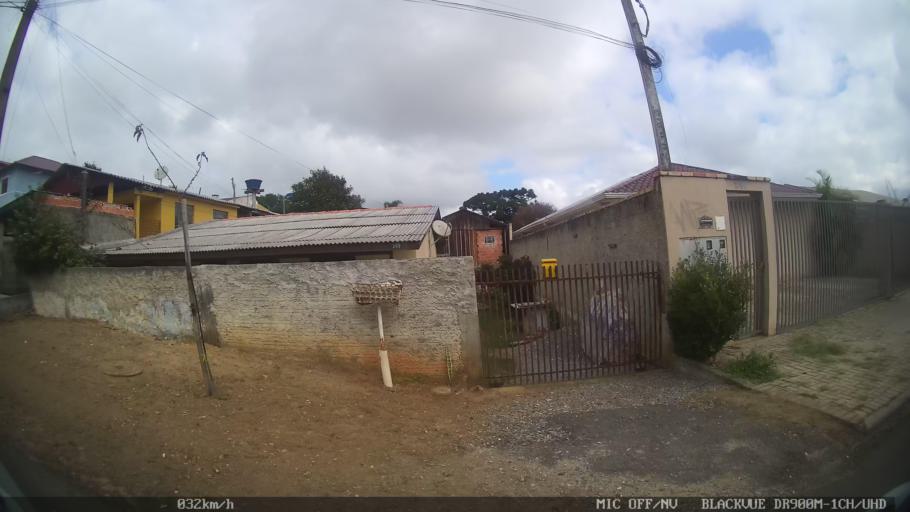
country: BR
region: Parana
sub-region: Almirante Tamandare
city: Almirante Tamandare
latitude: -25.3501
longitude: -49.2538
